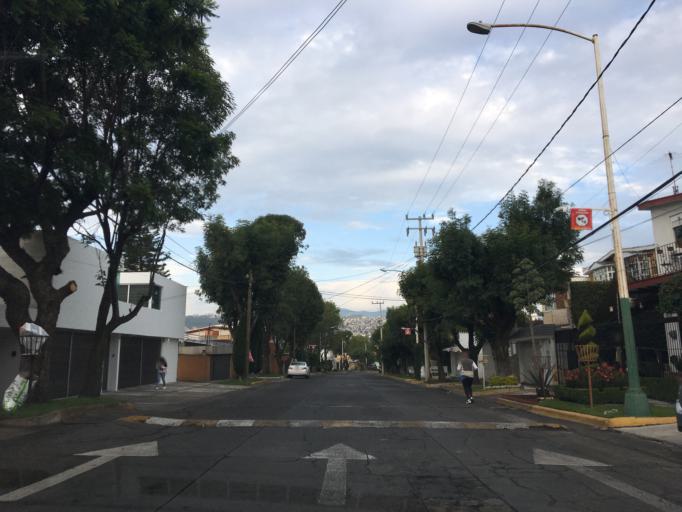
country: MX
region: Mexico
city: Naucalpan de Juarez
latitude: 19.4992
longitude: -99.2455
